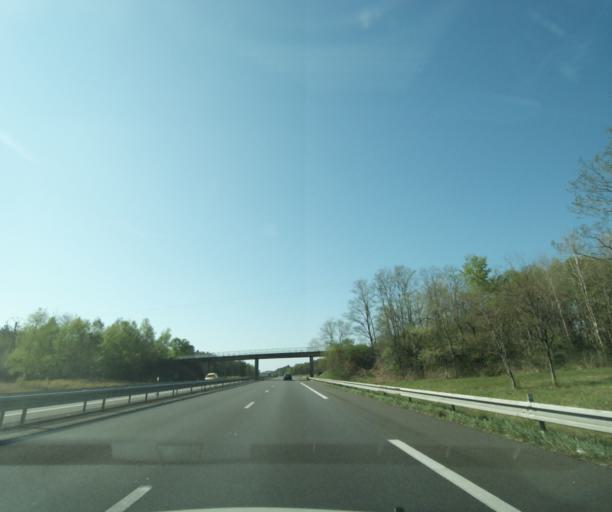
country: FR
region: Centre
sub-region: Departement du Loiret
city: Saint-Hilaire-Saint-Mesmin
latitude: 47.8011
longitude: 1.8504
